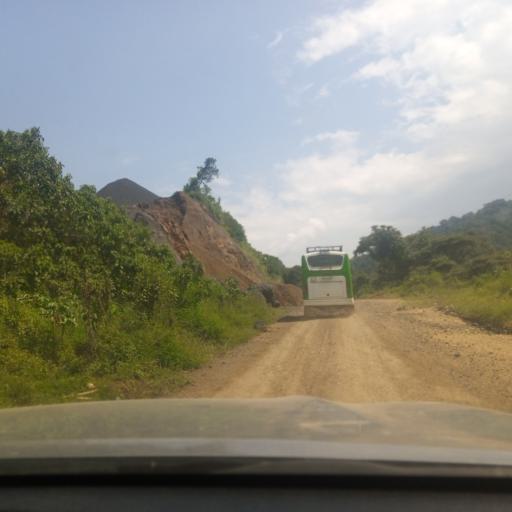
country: ET
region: Southern Nations, Nationalities, and People's Region
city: Tippi
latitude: 7.0699
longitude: 35.4403
